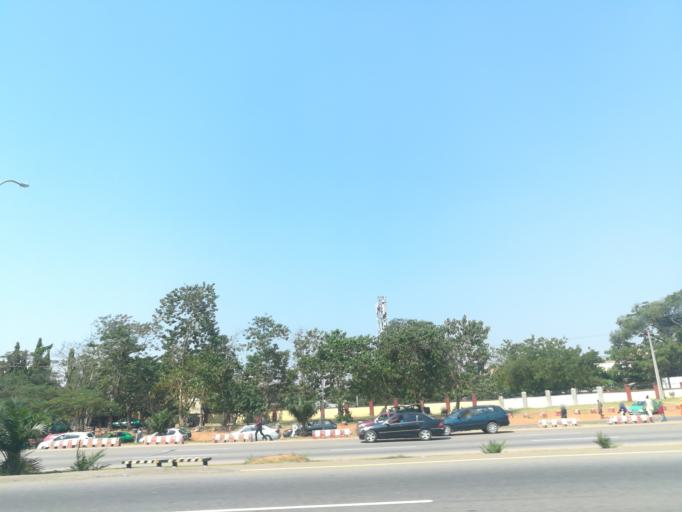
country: NG
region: Abuja Federal Capital Territory
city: Abuja
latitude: 9.0704
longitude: 7.4520
